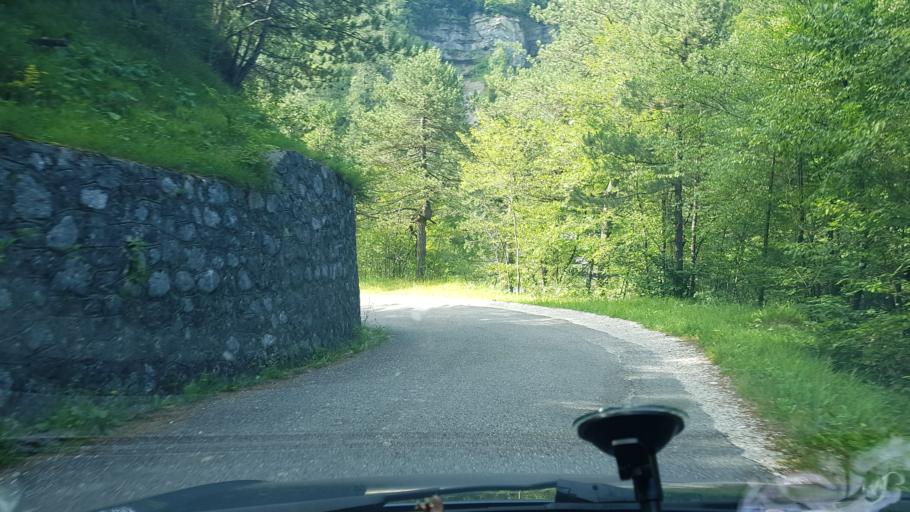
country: IT
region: Friuli Venezia Giulia
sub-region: Provincia di Udine
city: Prato
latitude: 46.3572
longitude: 13.3619
